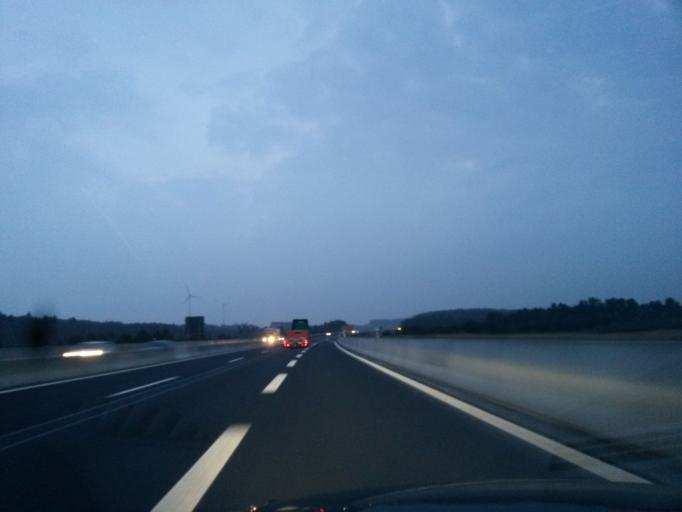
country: DE
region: Bavaria
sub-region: Regierungsbezirk Unterfranken
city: Rannungen
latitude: 50.1984
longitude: 10.2152
